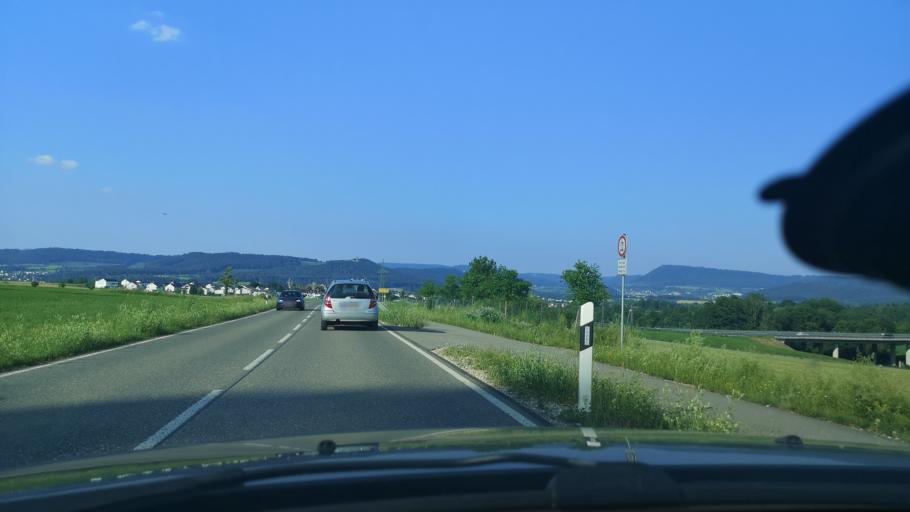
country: DE
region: Baden-Wuerttemberg
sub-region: Regierungsbezirk Stuttgart
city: Salach
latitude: 48.6681
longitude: 9.7299
